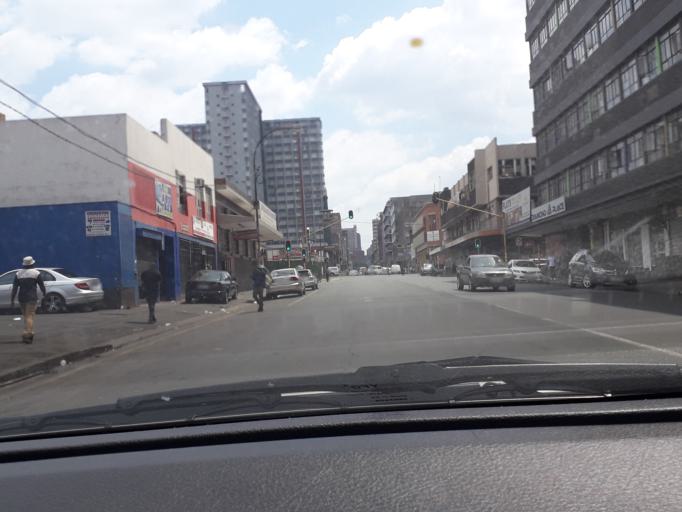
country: ZA
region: Gauteng
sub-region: City of Johannesburg Metropolitan Municipality
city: Johannesburg
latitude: -26.2055
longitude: 28.0529
